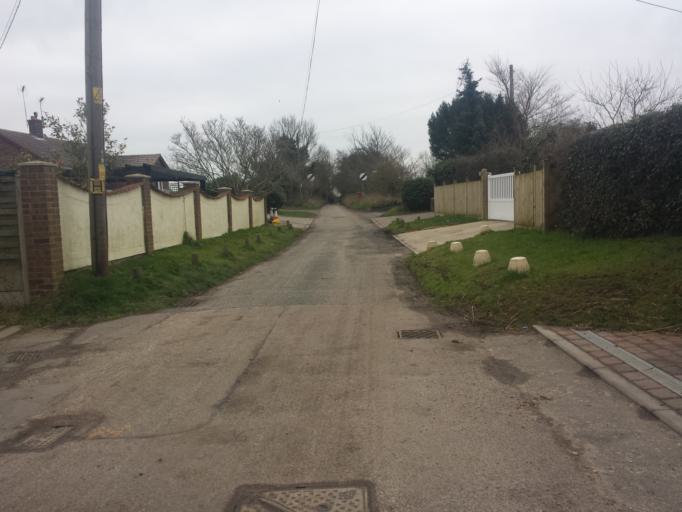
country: GB
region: England
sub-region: Essex
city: Frinton-on-Sea
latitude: 51.9031
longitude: 1.1898
